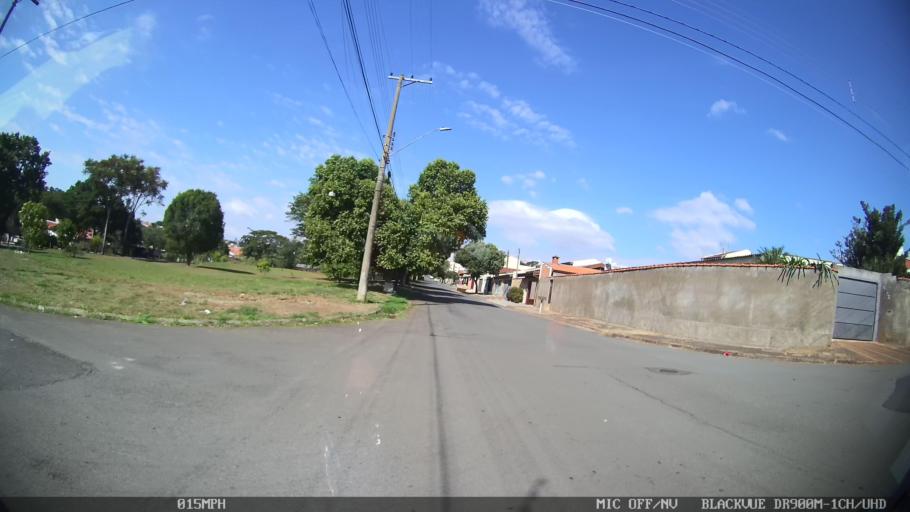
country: BR
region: Sao Paulo
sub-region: Americana
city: Americana
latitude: -22.7188
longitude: -47.3062
